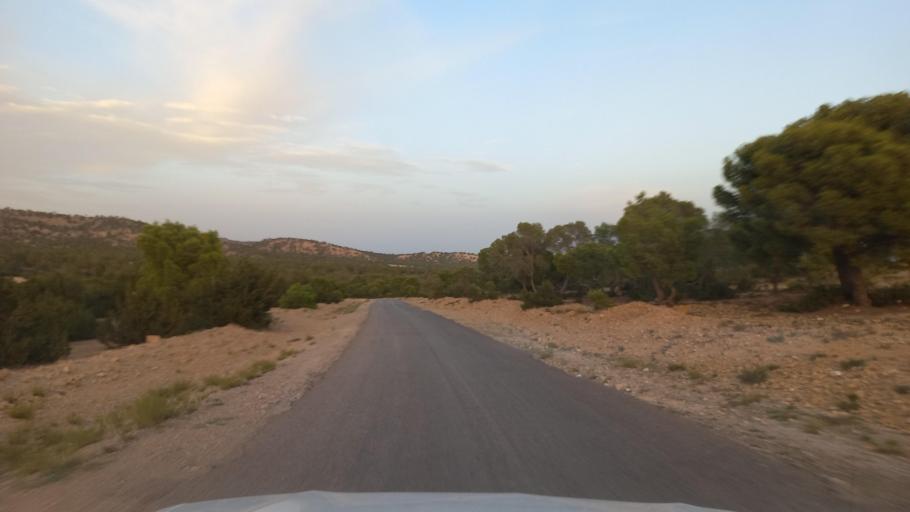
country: TN
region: Al Qasrayn
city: Sbiba
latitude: 35.4123
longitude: 8.9385
